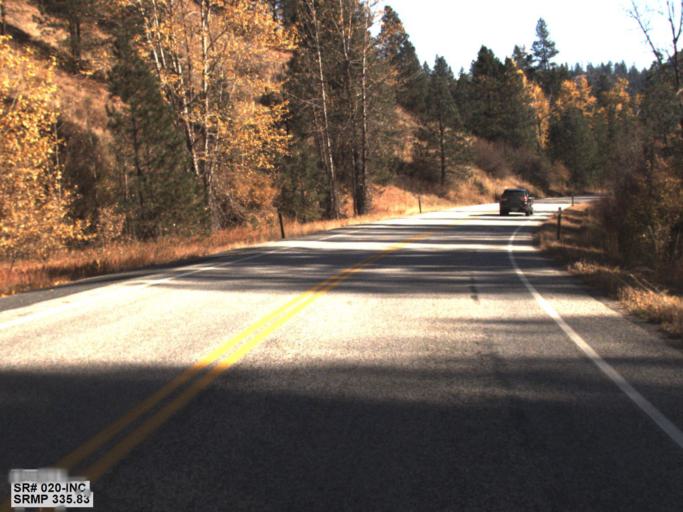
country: US
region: Washington
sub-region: Stevens County
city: Kettle Falls
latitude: 48.5850
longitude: -118.2107
